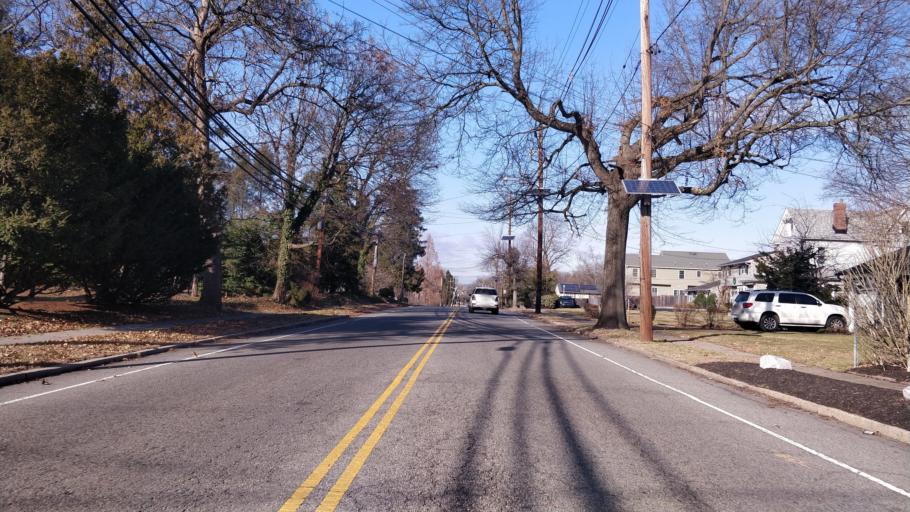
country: US
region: New Jersey
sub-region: Middlesex County
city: South Plainfield
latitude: 40.5884
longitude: -74.4328
